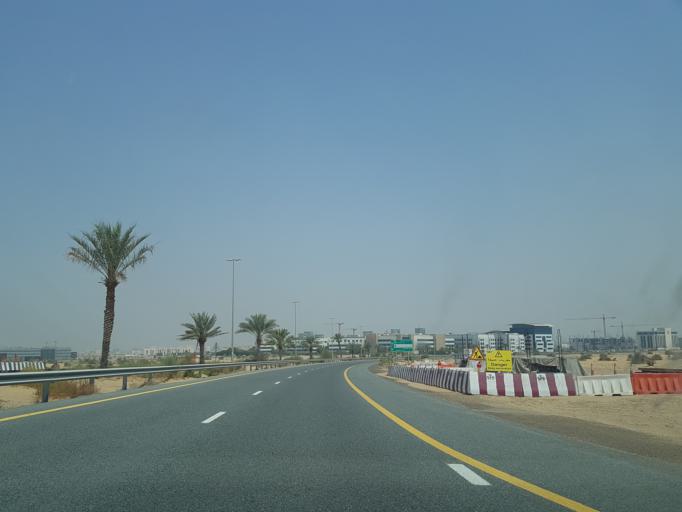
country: AE
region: Ash Shariqah
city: Sharjah
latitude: 25.1189
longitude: 55.4280
